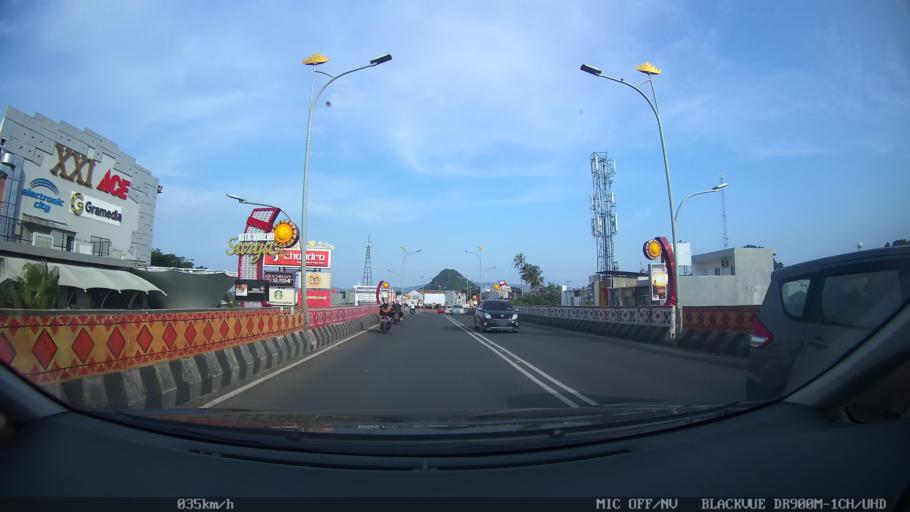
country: ID
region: Lampung
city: Kedaton
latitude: -5.3826
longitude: 105.2589
